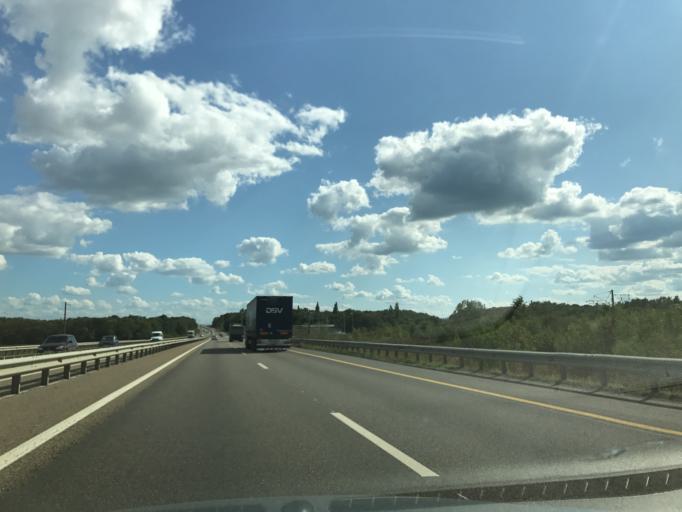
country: RU
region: Krasnodarskiy
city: Saratovskaya
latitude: 44.7958
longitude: 39.2325
